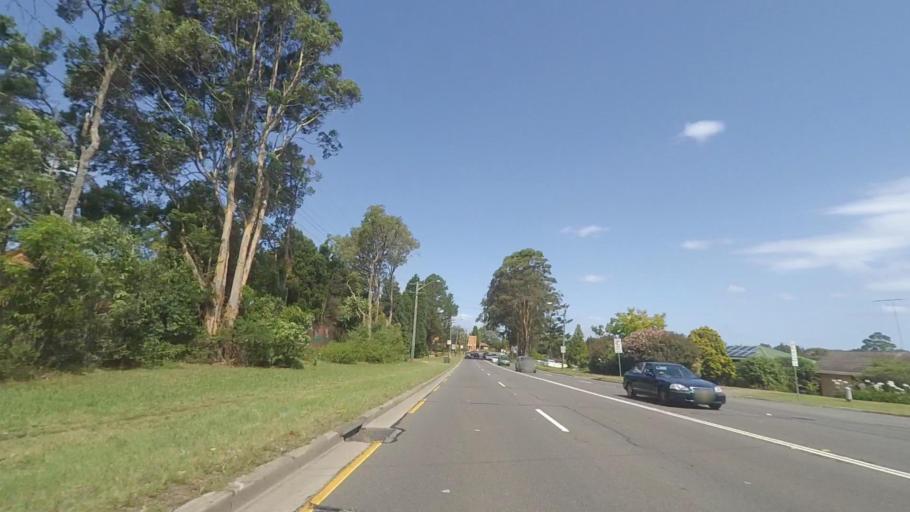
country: AU
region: New South Wales
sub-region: Parramatta
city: Carlingford
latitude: -33.7689
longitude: 151.0491
